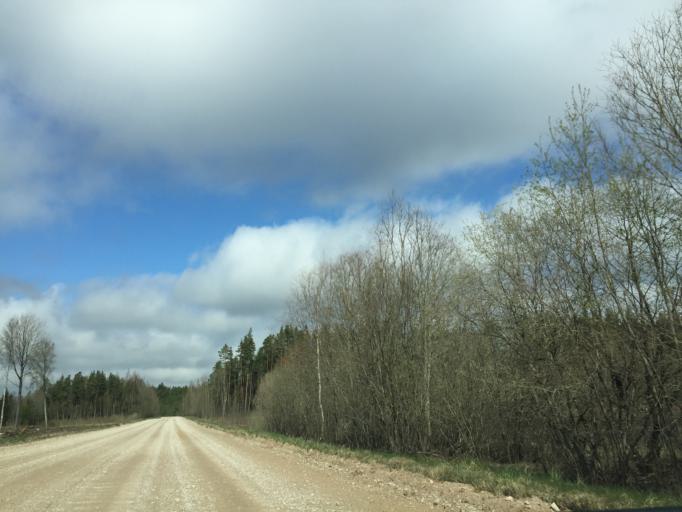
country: LV
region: Apes Novads
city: Ape
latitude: 57.4881
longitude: 26.4272
